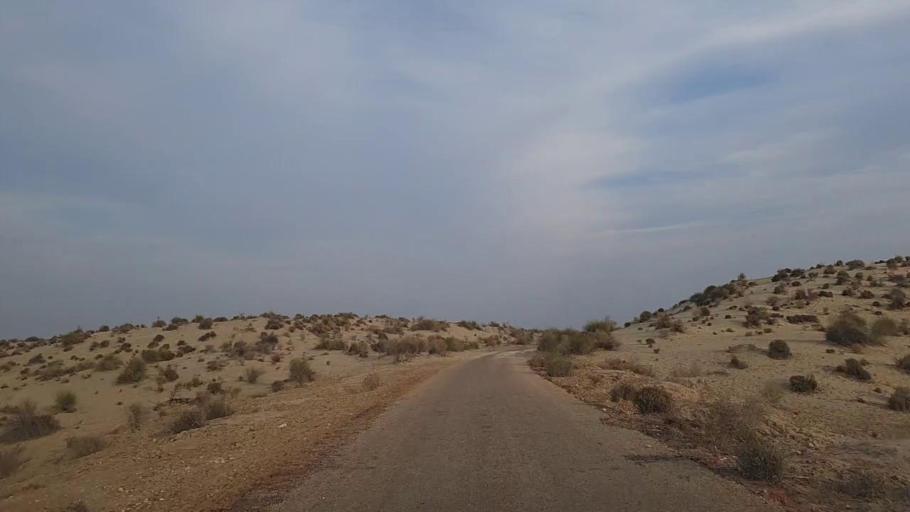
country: PK
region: Sindh
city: Jam Sahib
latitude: 26.4914
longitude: 68.5514
